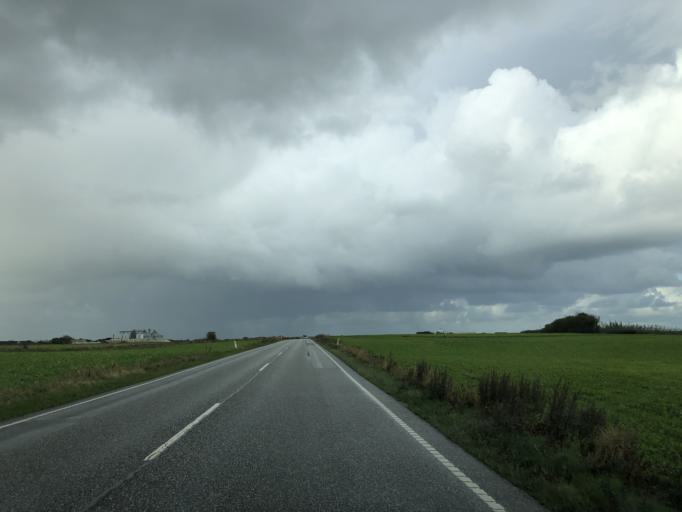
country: DK
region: Central Jutland
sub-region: Lemvig Kommune
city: Harboore
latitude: 56.5542
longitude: 8.1995
